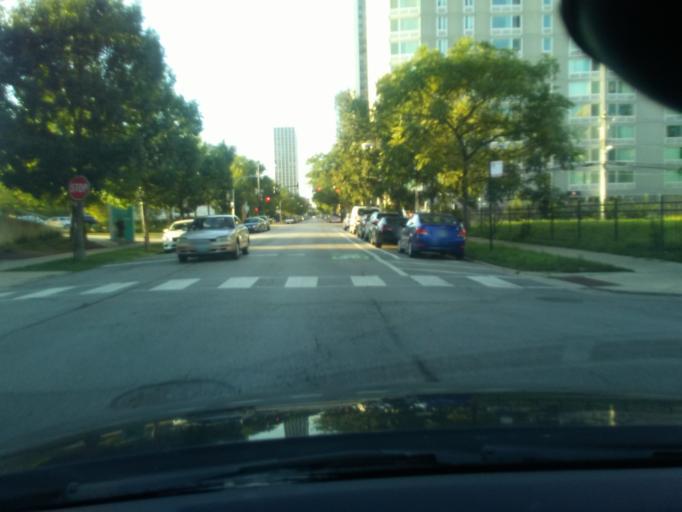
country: US
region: Illinois
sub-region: Cook County
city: Evanston
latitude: 41.9665
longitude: -87.6501
